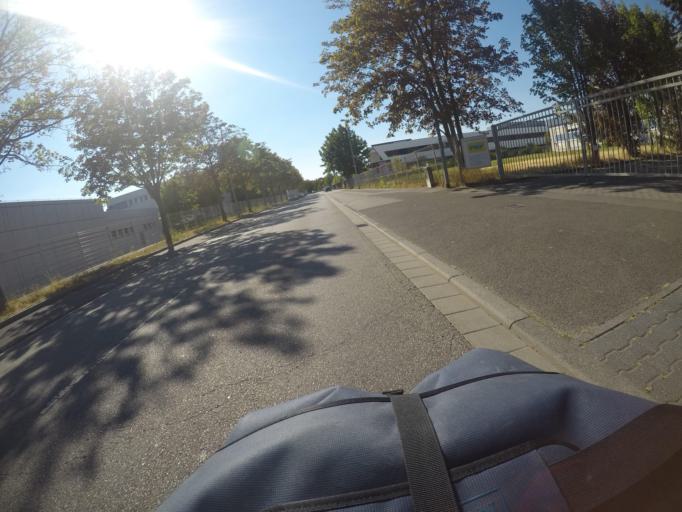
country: DE
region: Hesse
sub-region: Regierungsbezirk Darmstadt
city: Hochheim am Main
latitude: 50.0574
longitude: 8.3318
